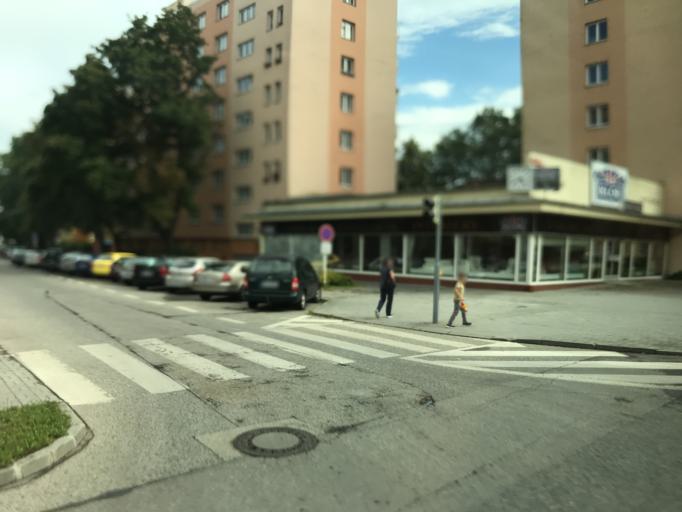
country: CZ
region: Jihocesky
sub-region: Okres Ceske Budejovice
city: Ceske Budejovice
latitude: 48.9611
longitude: 14.4726
